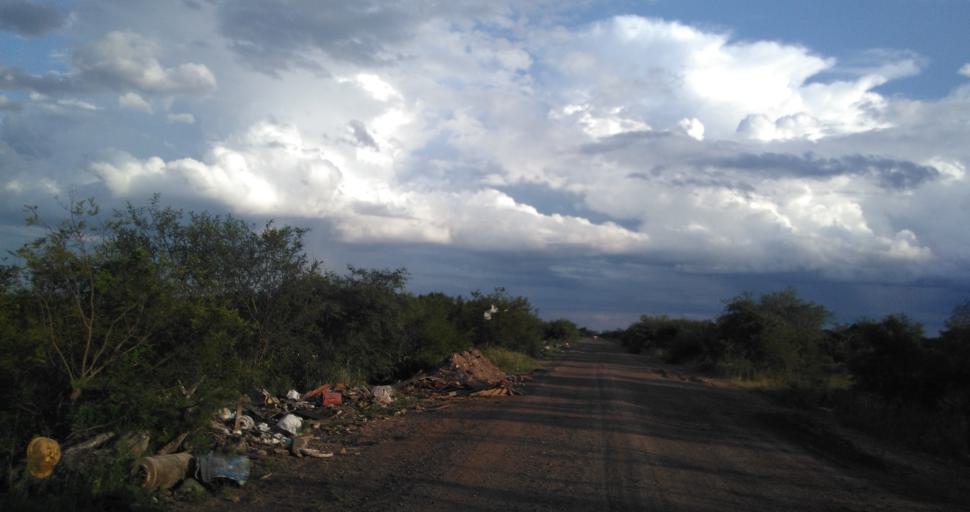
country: AR
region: Chaco
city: Resistencia
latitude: -27.4168
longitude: -58.9391
